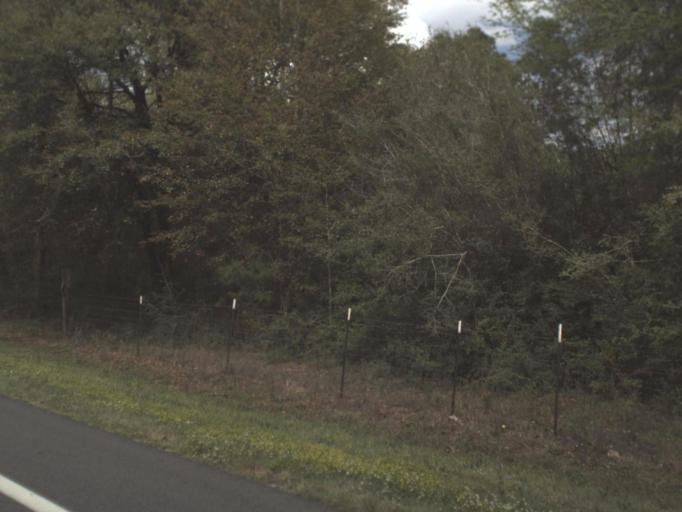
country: US
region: Alabama
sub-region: Covington County
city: Florala
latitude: 30.9360
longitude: -86.4787
